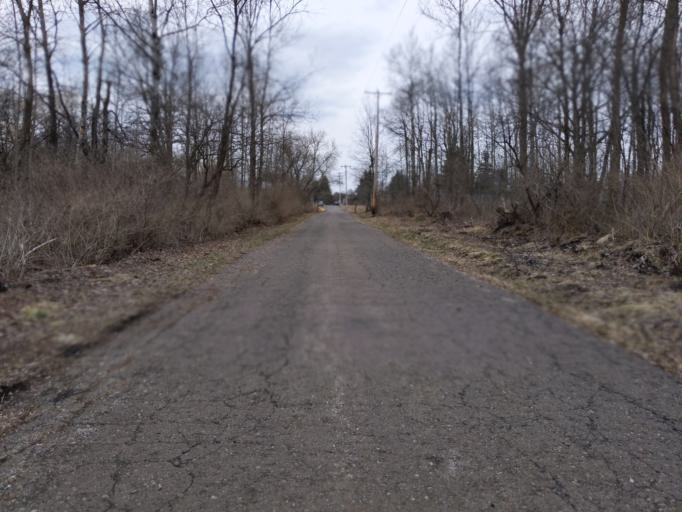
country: US
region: New York
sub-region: Tompkins County
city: Dryden
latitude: 42.5107
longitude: -76.3436
